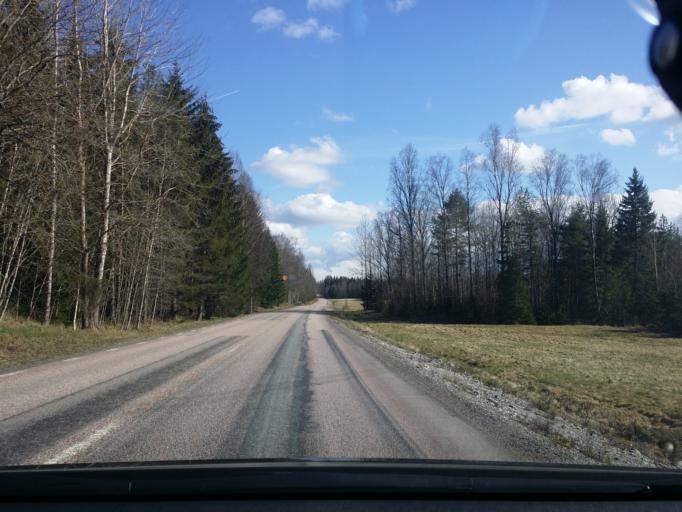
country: SE
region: Vaestmanland
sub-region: Sala Kommun
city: Sala
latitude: 59.9809
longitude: 16.4891
